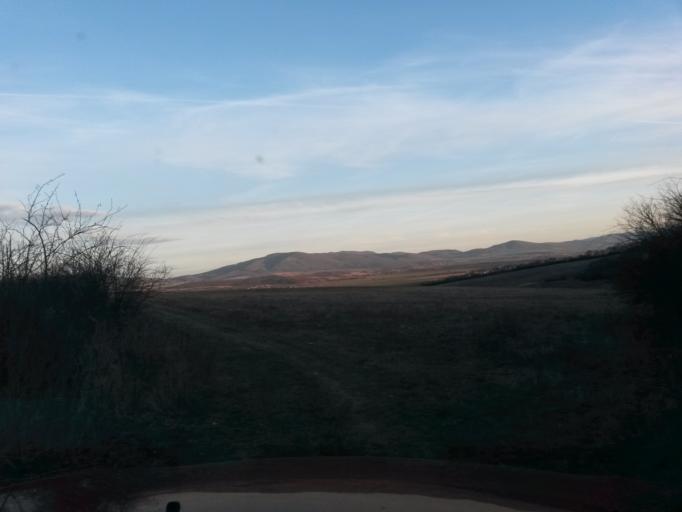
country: SK
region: Kosicky
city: Kosice
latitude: 48.7075
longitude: 21.3091
